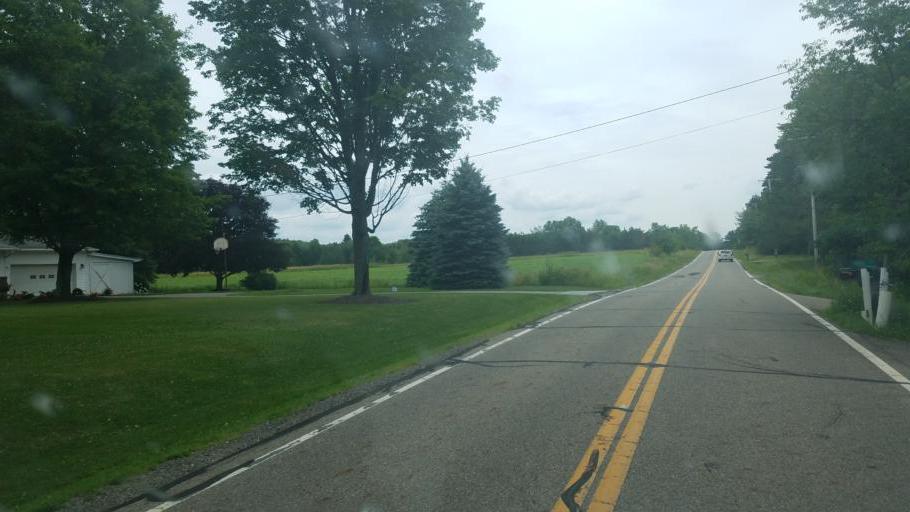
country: US
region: Ohio
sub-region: Geauga County
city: Burton
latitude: 41.4981
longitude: -81.1744
